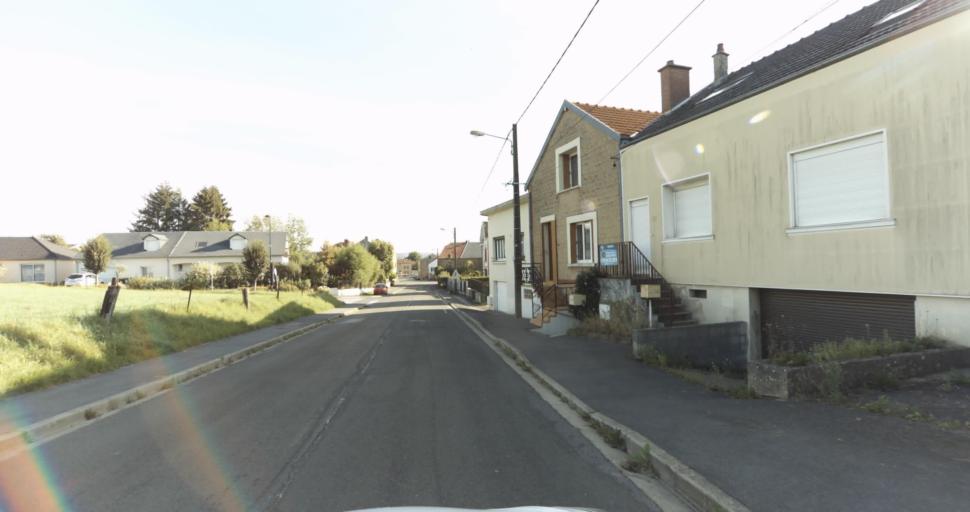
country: FR
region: Champagne-Ardenne
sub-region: Departement des Ardennes
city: Villers-Semeuse
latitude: 49.7383
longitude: 4.7464
